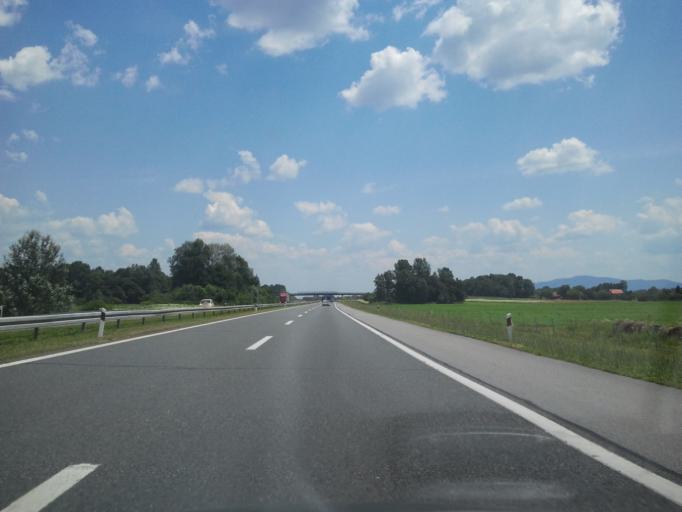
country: HR
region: Brodsko-Posavska
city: Resetari
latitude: 45.2237
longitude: 17.4875
